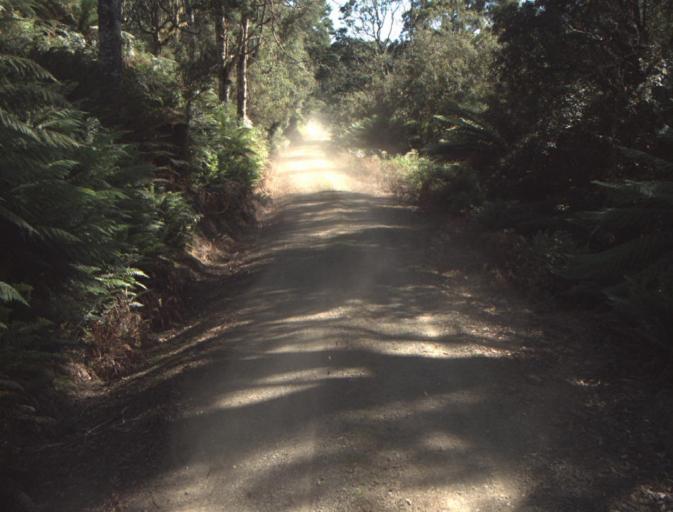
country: AU
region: Tasmania
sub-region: Dorset
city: Scottsdale
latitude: -41.2758
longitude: 147.3624
